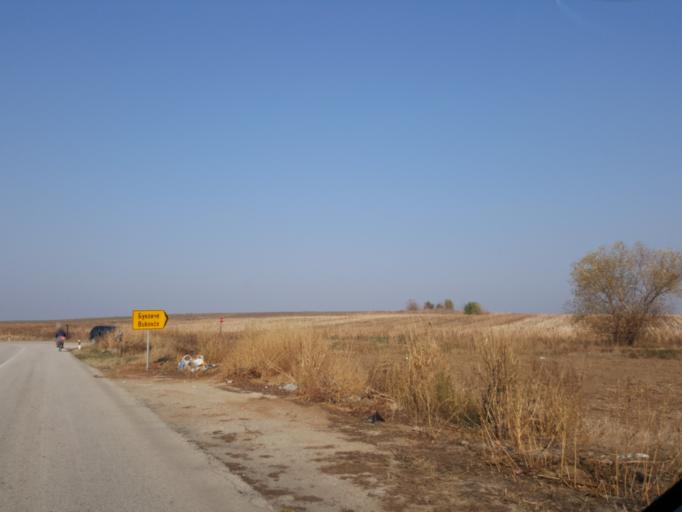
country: RS
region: Central Serbia
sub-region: Borski Okrug
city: Negotin
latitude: 44.2075
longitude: 22.5851
